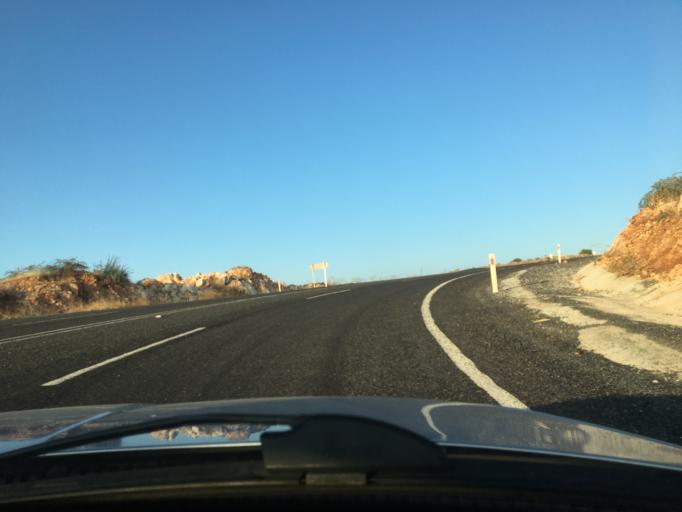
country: TR
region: Sanliurfa
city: Halfeti
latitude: 37.2405
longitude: 37.8827
